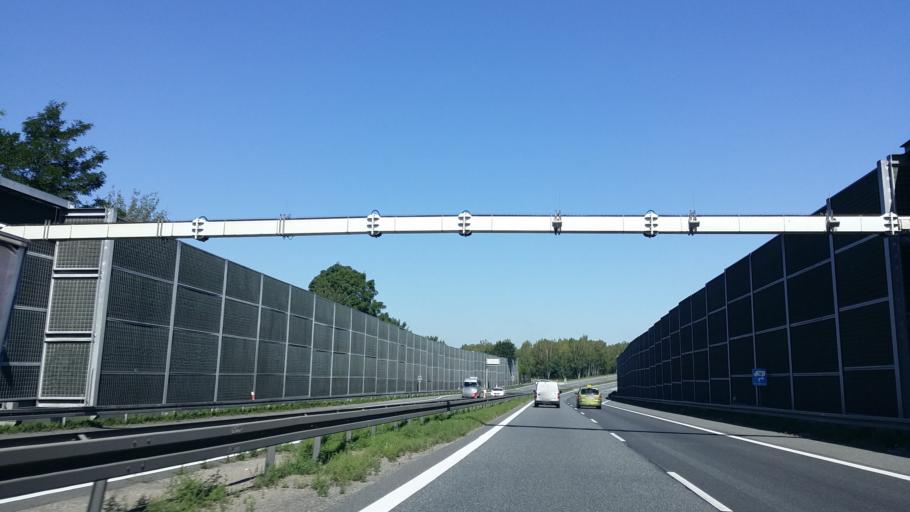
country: PL
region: Silesian Voivodeship
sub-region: Myslowice
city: Myslowice
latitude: 50.2029
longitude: 19.1672
